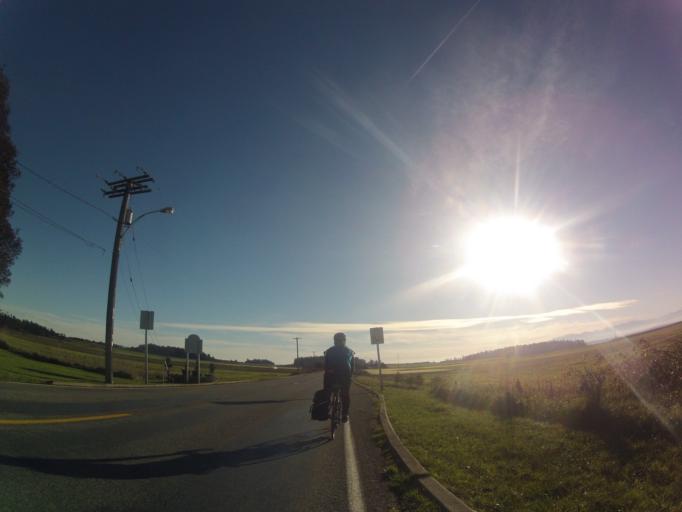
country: US
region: Washington
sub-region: Island County
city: Coupeville
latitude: 48.2038
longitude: -122.6863
